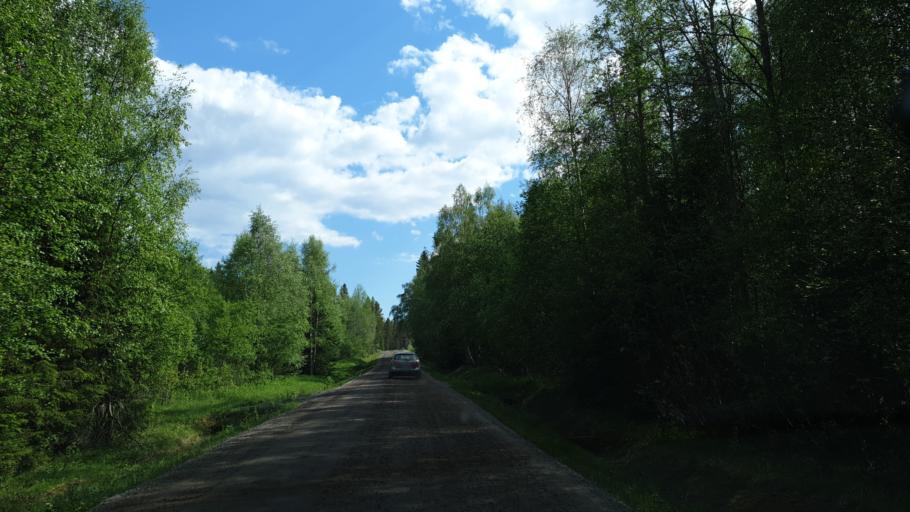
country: SE
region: Vaesterbotten
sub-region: Robertsfors Kommun
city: Robertsfors
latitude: 64.0350
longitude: 20.8833
